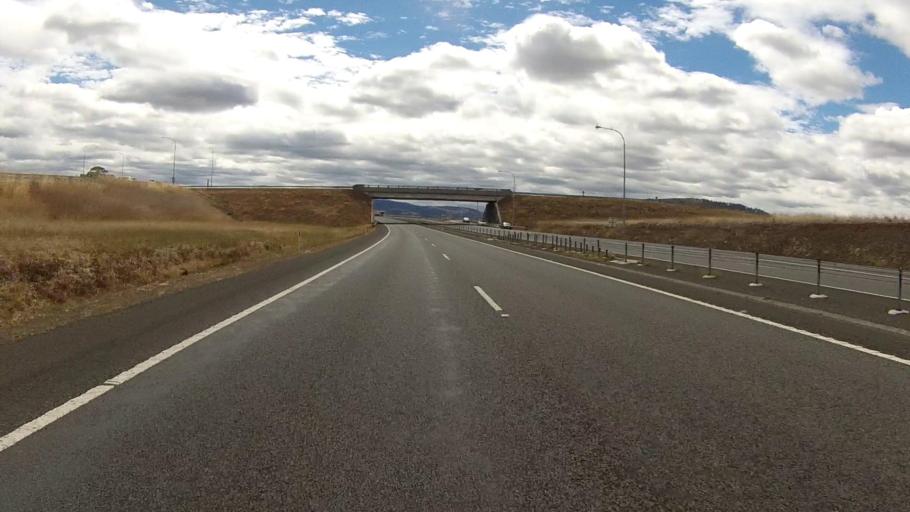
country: AU
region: Tasmania
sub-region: Brighton
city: Bridgewater
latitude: -42.7150
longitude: 147.2433
